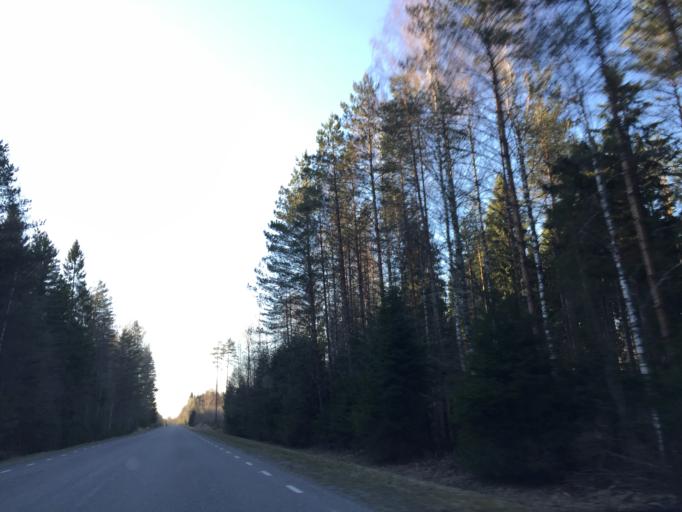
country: EE
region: Ida-Virumaa
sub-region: Toila vald
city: Voka
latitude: 59.1699
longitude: 27.5760
